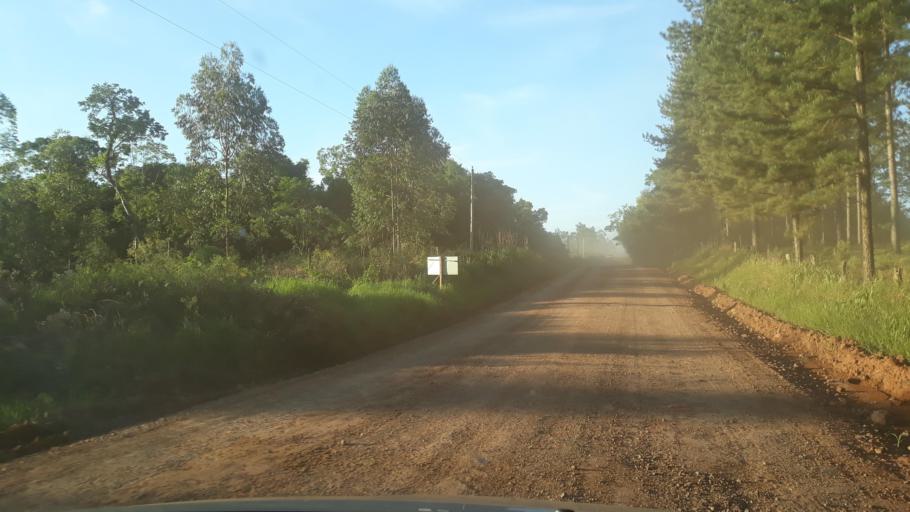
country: AR
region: Misiones
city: Ruiz de Montoya
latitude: -27.0555
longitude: -55.0048
